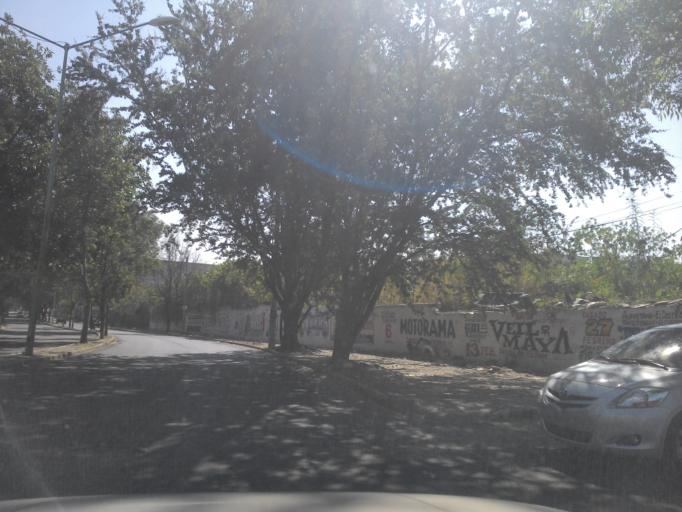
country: MX
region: Jalisco
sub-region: Zapopan
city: Zapopan
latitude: 20.7042
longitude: -103.3584
